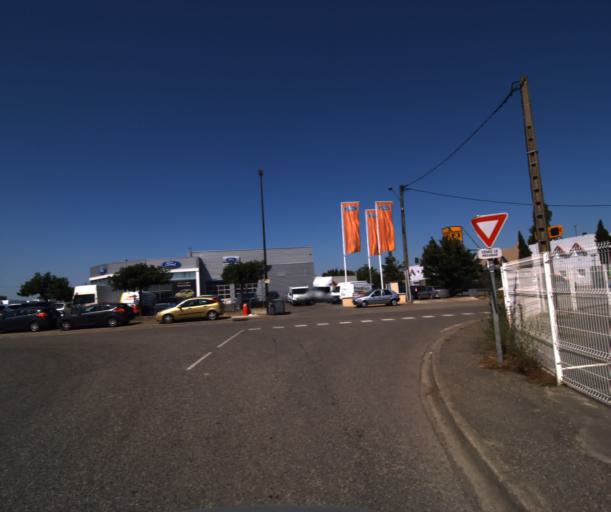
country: FR
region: Midi-Pyrenees
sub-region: Departement de la Haute-Garonne
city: Saubens
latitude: 43.4910
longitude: 1.3435
